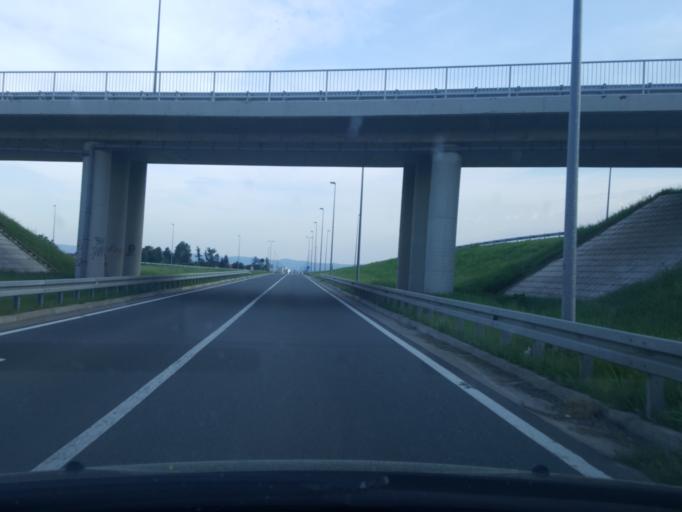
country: RS
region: Autonomna Pokrajina Vojvodina
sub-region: Juznobacki Okrug
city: Novi Sad
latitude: 45.3058
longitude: 19.8078
